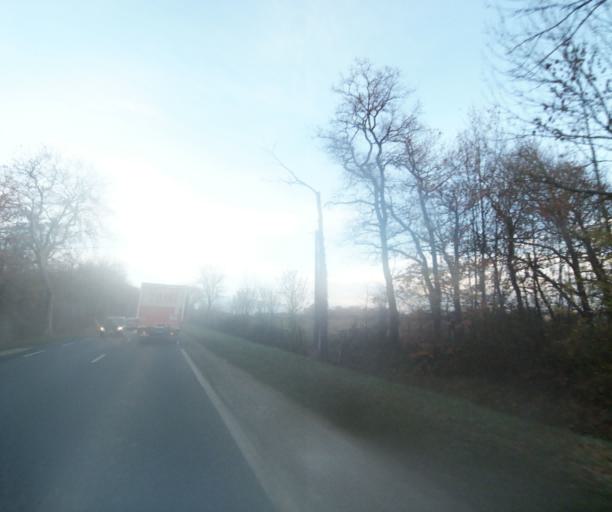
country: FR
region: Poitou-Charentes
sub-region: Departement de la Charente-Maritime
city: Fontcouverte
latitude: 45.7820
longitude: -0.5707
